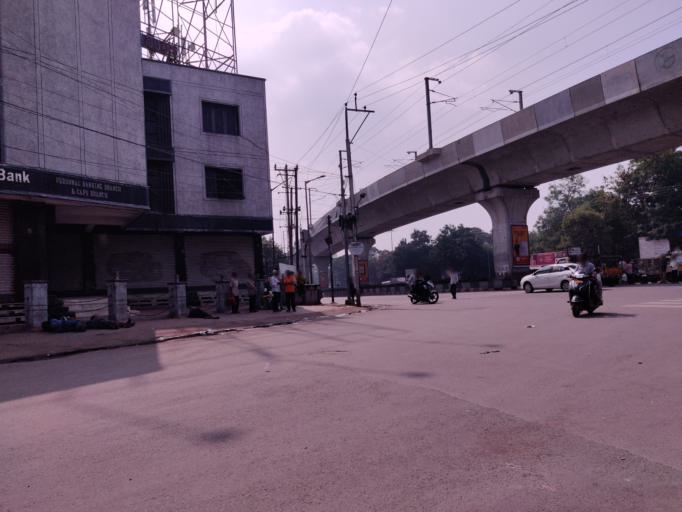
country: IN
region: Telangana
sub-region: Hyderabad
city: Hyderabad
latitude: 17.3961
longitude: 78.4713
